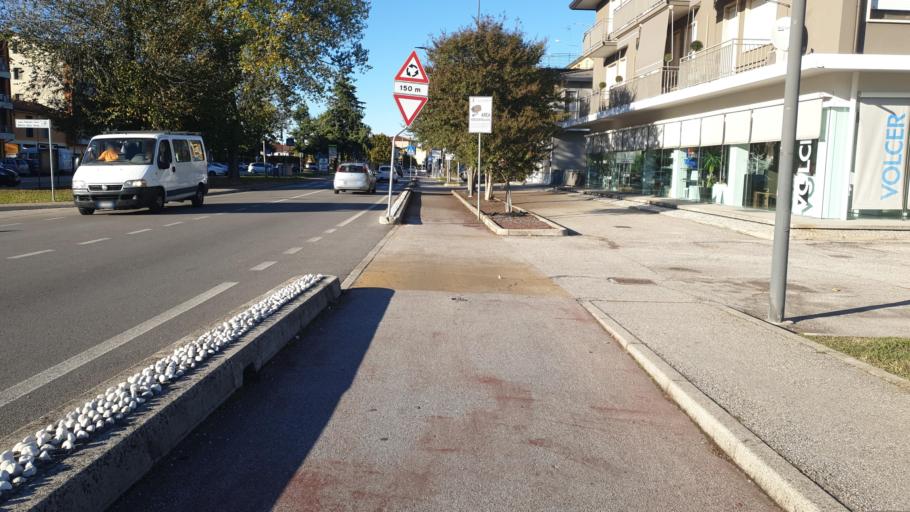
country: IT
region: Veneto
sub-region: Provincia di Venezia
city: Cazzago-Ex Polo
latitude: 45.4382
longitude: 12.0747
